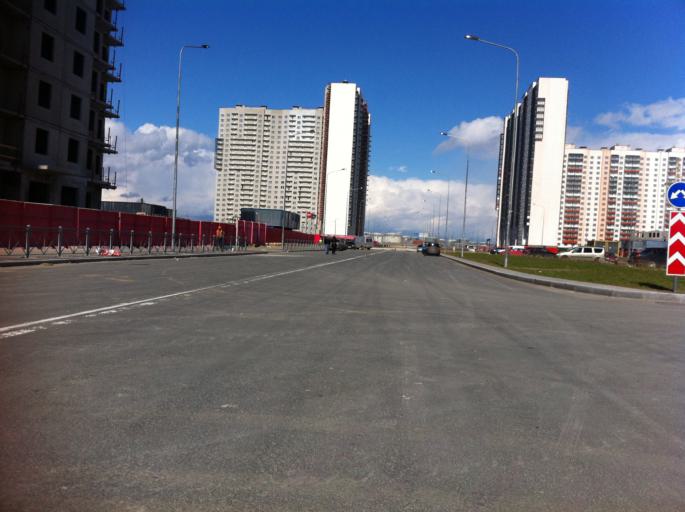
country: RU
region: St.-Petersburg
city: Uritsk
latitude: 59.8672
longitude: 30.1573
